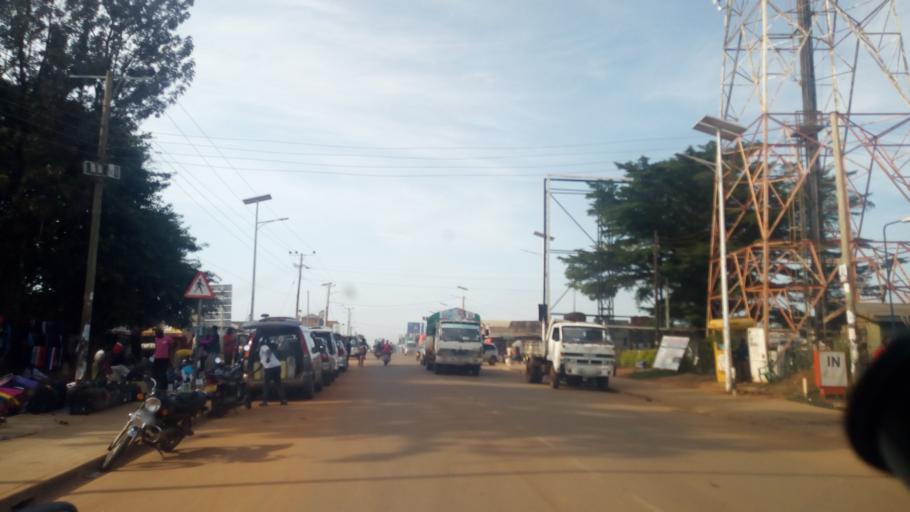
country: UG
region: Northern Region
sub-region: Gulu District
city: Gulu
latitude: 2.7681
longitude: 32.2985
